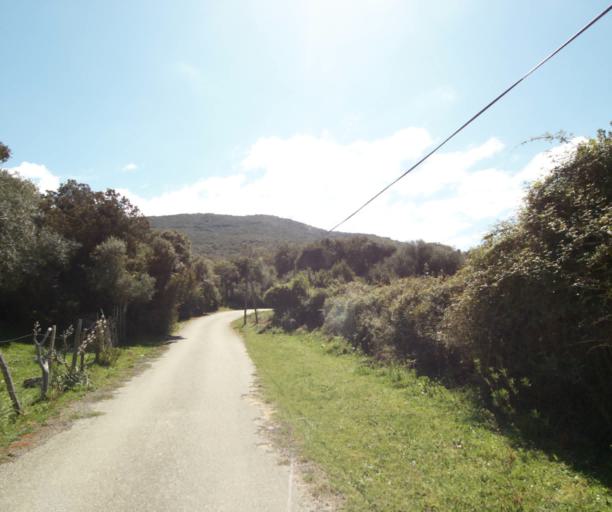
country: FR
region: Corsica
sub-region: Departement de la Corse-du-Sud
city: Propriano
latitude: 41.6420
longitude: 8.8705
